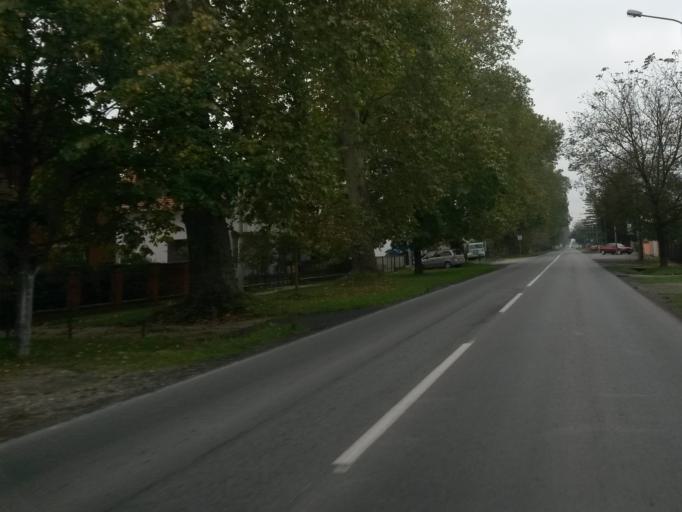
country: HR
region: Osjecko-Baranjska
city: Visnjevac
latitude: 45.5293
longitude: 18.6100
